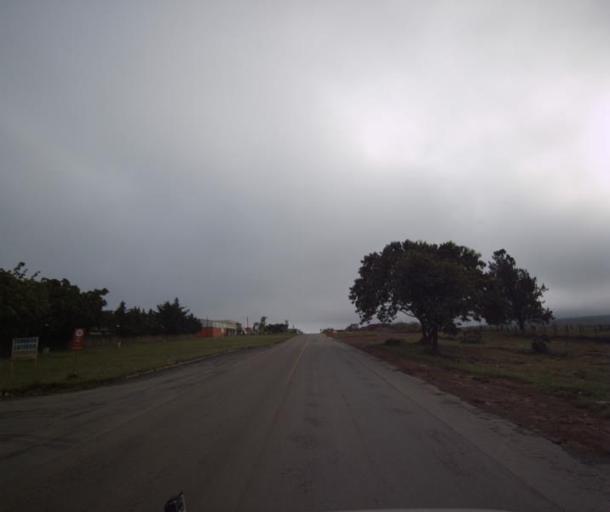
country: BR
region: Goias
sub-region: Pirenopolis
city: Pirenopolis
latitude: -15.7792
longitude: -48.7663
